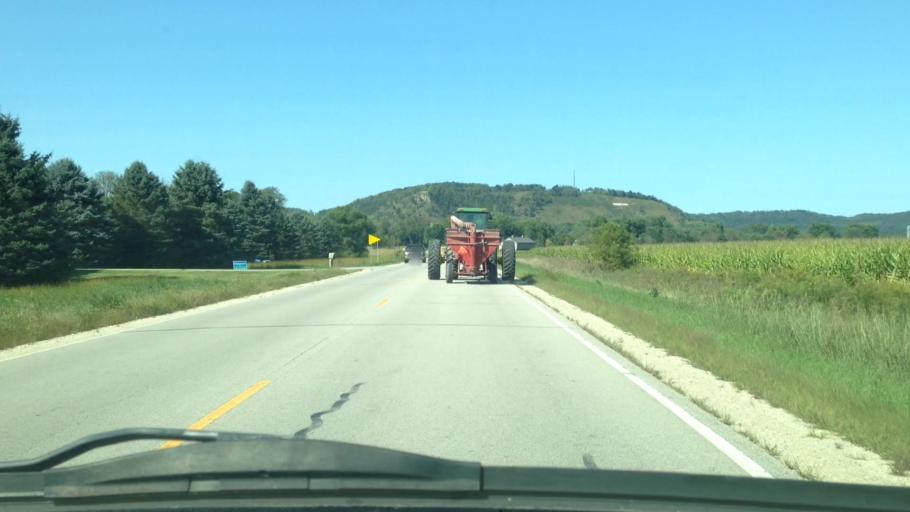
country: US
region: Minnesota
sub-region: Fillmore County
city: Rushford
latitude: 43.7888
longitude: -91.7653
